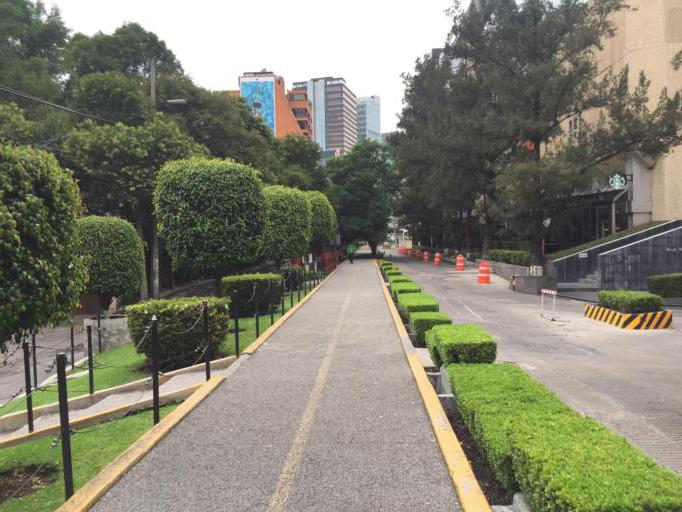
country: MX
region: Mexico City
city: Miguel Hidalgo
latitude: 19.4298
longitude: -99.2067
